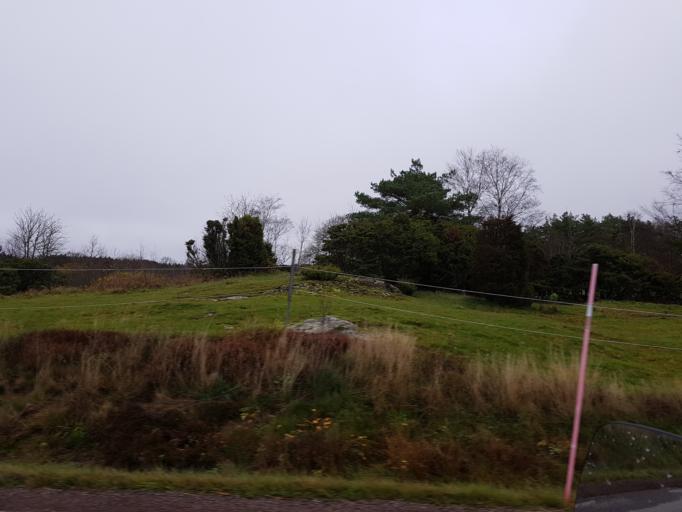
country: SE
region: Vaestra Goetaland
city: Svanesund
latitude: 58.1619
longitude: 11.7689
